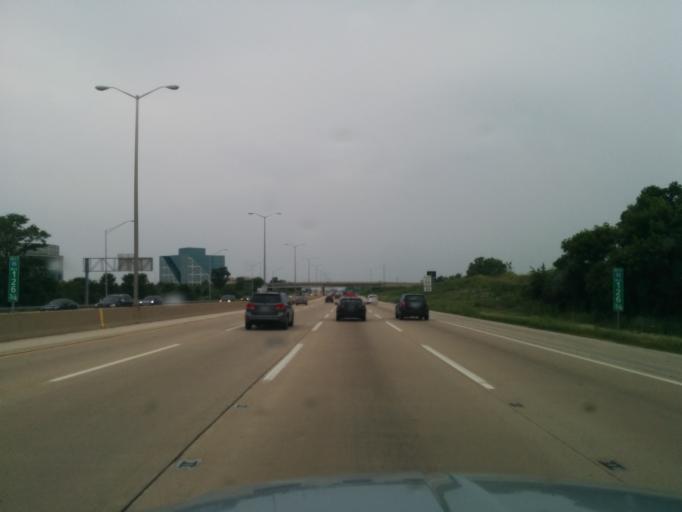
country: US
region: Illinois
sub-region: DuPage County
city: Naperville
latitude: 41.8064
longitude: -88.1371
